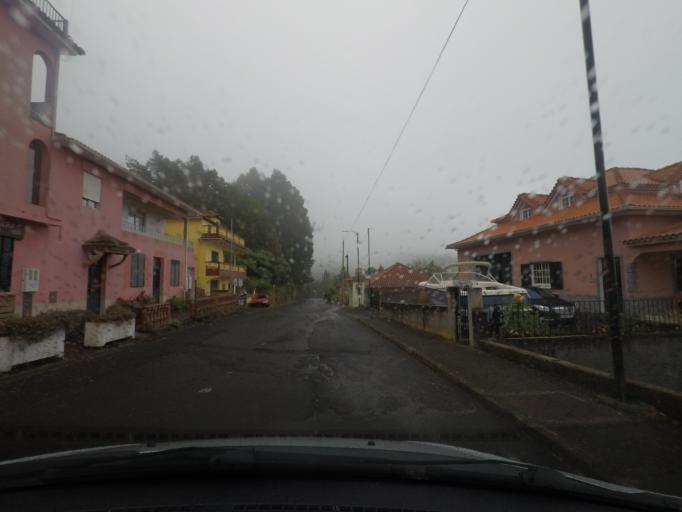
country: PT
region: Madeira
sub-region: Santana
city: Santana
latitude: 32.7959
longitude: -16.8663
